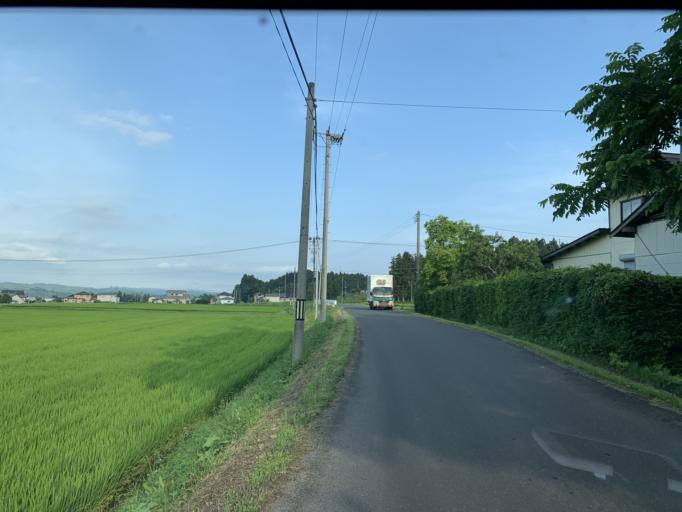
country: JP
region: Iwate
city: Ichinoseki
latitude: 38.8420
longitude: 141.1563
